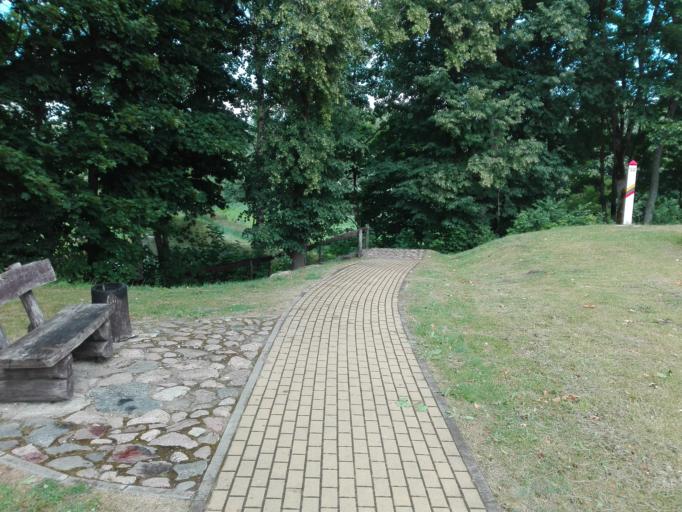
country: LT
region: Panevezys
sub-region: Birzai
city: Birzai
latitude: 56.4002
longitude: 24.7696
